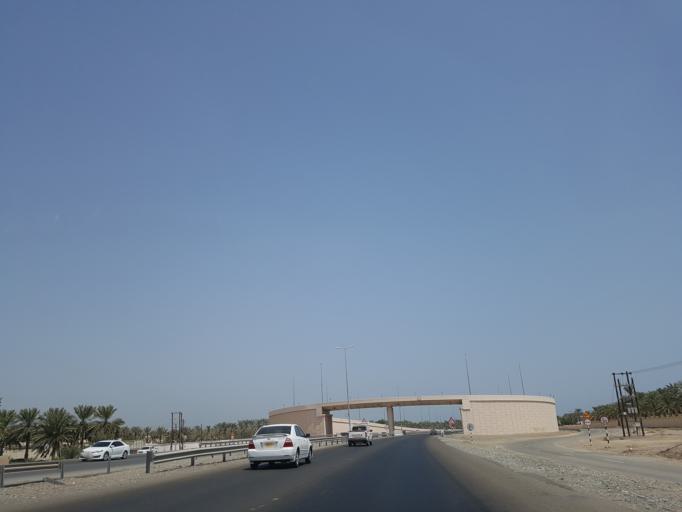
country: OM
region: Al Batinah
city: Saham
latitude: 24.1791
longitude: 56.8569
